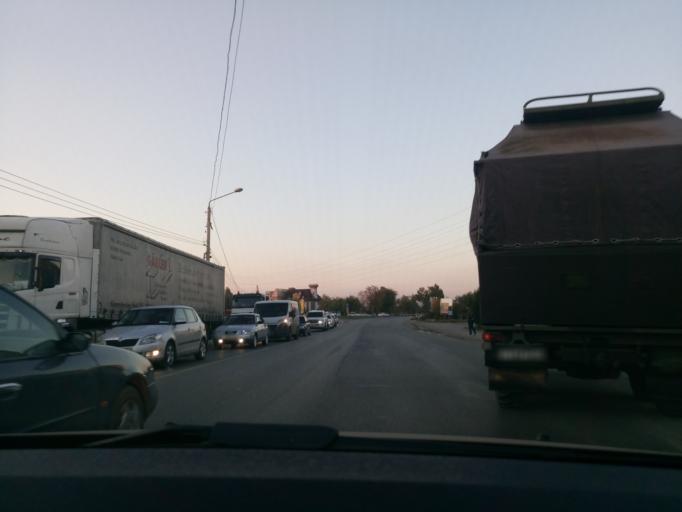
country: RU
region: Rostov
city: Kalinin
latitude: 47.2515
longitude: 39.6142
